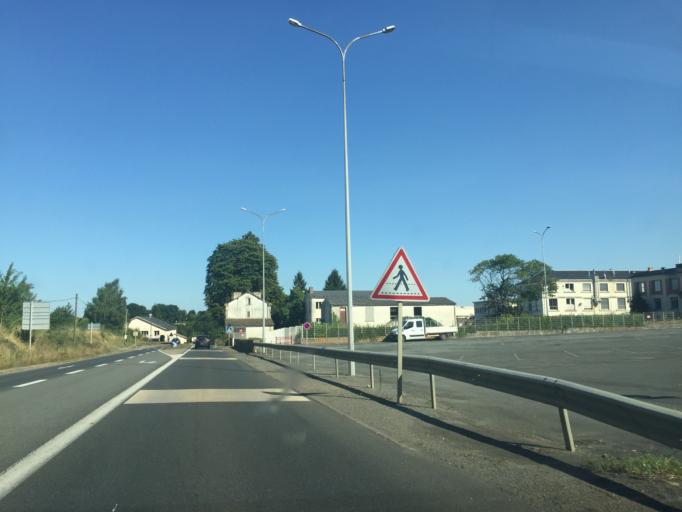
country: FR
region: Poitou-Charentes
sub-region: Departement des Deux-Sevres
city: Melle
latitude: 46.2194
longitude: -0.1339
